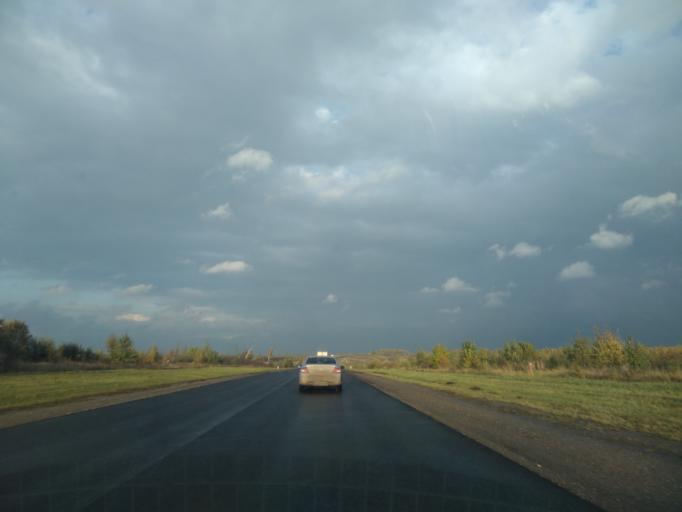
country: RU
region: Lipetsk
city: Donskoye
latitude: 52.5804
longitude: 38.8066
